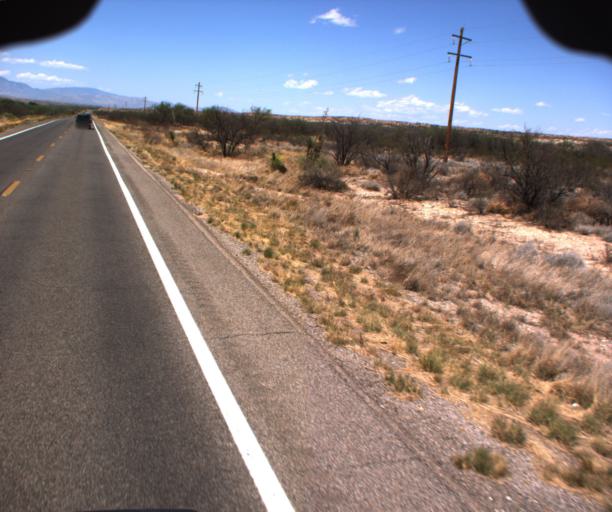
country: US
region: Arizona
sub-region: Cochise County
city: Saint David
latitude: 31.8416
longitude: -110.1905
